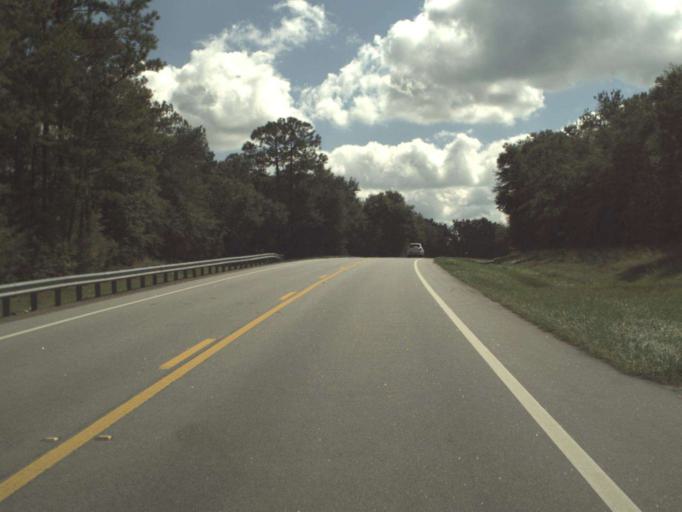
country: US
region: Florida
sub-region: Walton County
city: Freeport
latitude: 30.5757
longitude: -85.9268
